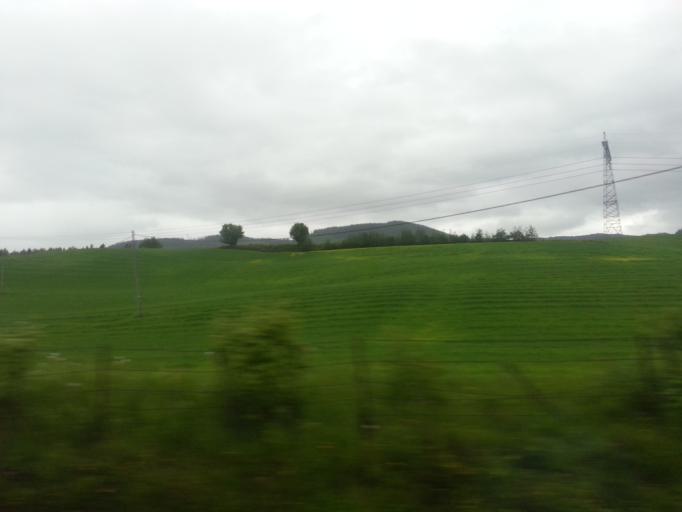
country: NO
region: Sor-Trondelag
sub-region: Melhus
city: Melhus
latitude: 63.3215
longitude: 10.3393
